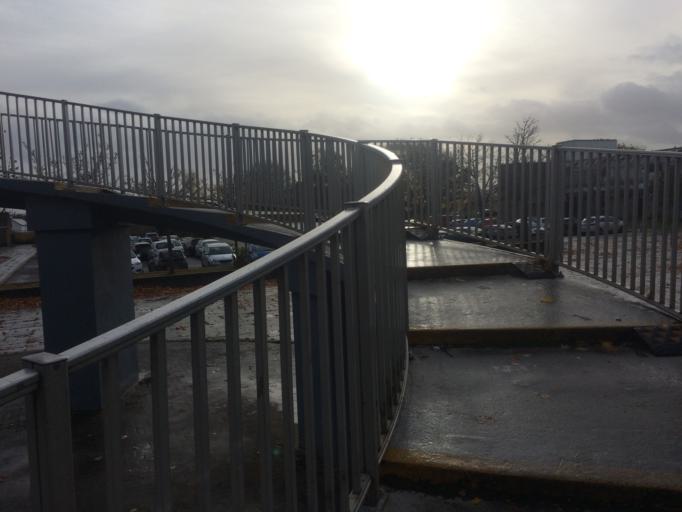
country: GB
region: Scotland
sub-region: Highland
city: Alness
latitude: 57.6942
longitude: -4.2508
